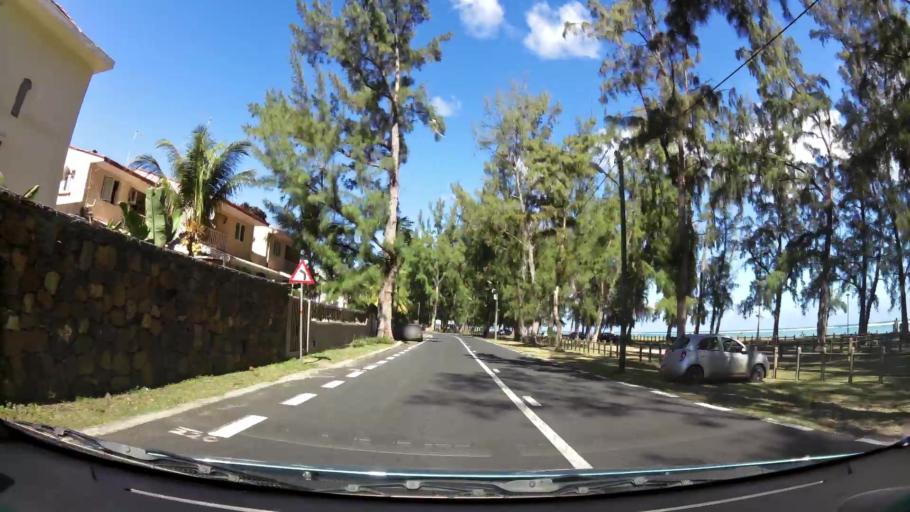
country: MU
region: Black River
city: Flic en Flac
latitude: -20.2887
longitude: 57.3637
